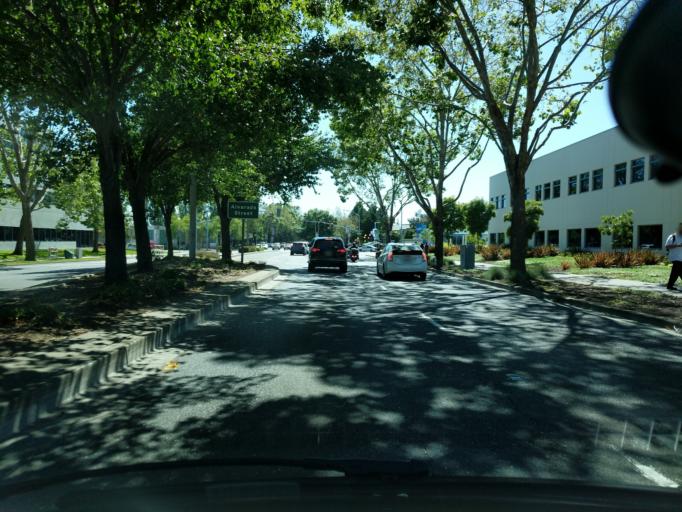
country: US
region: California
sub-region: Alameda County
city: San Leandro
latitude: 37.7235
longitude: -122.1626
